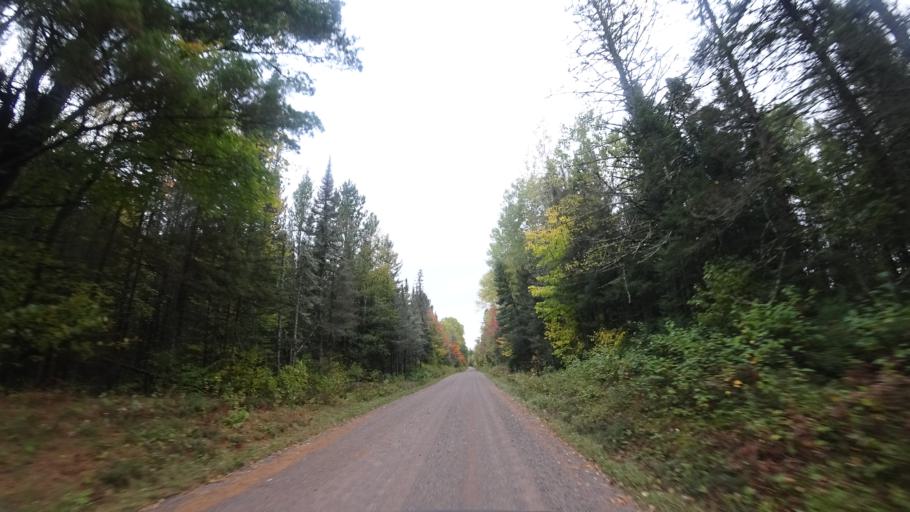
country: US
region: Wisconsin
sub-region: Sawyer County
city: Little Round Lake
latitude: 46.0709
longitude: -90.9939
